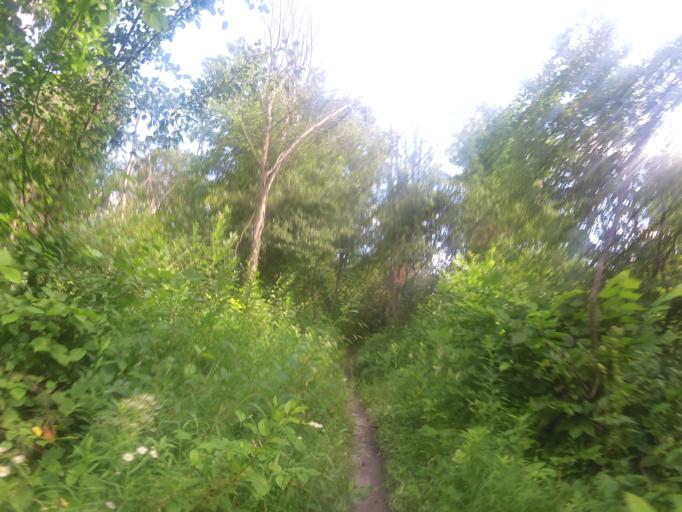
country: CA
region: Ontario
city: Bells Corners
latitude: 45.3301
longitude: -75.8005
